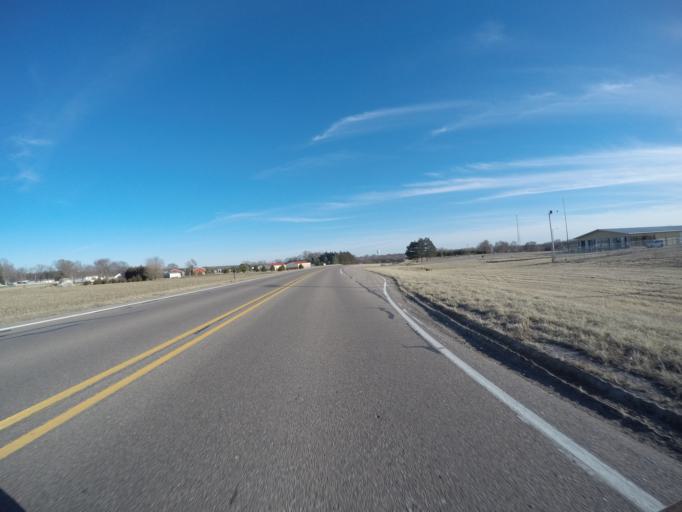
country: US
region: Nebraska
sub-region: Gage County
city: Wymore
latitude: 40.1375
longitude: -96.6748
